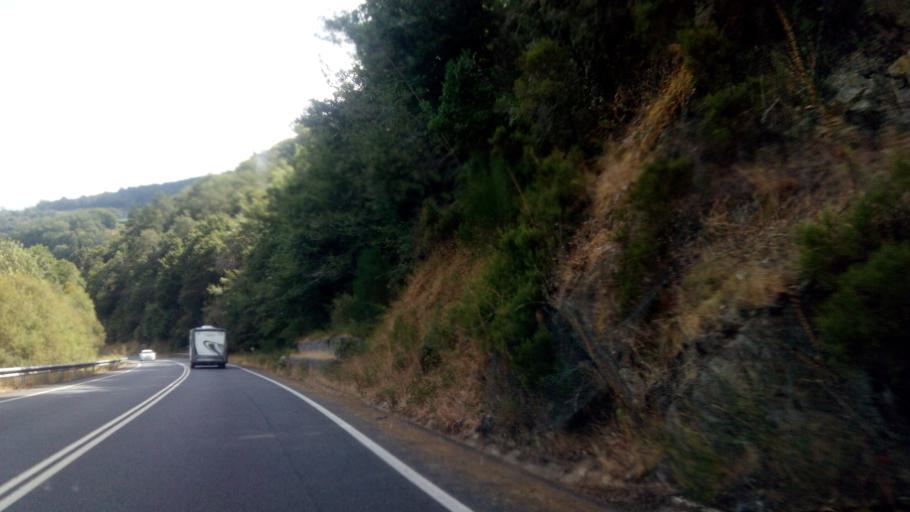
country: ES
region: Galicia
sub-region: Provincia de Ourense
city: Nogueira de Ramuin
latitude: 42.4288
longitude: -7.7576
